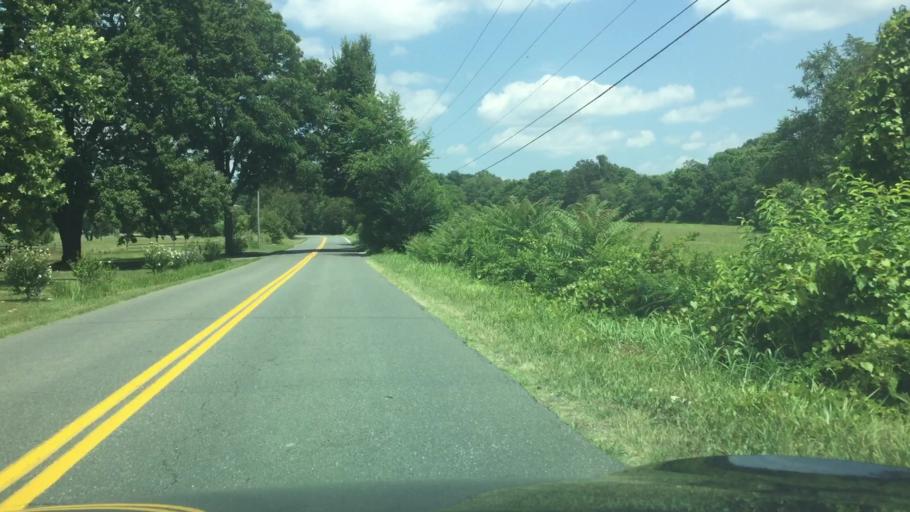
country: US
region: Virginia
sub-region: Campbell County
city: Concord
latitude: 37.3472
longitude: -78.9150
